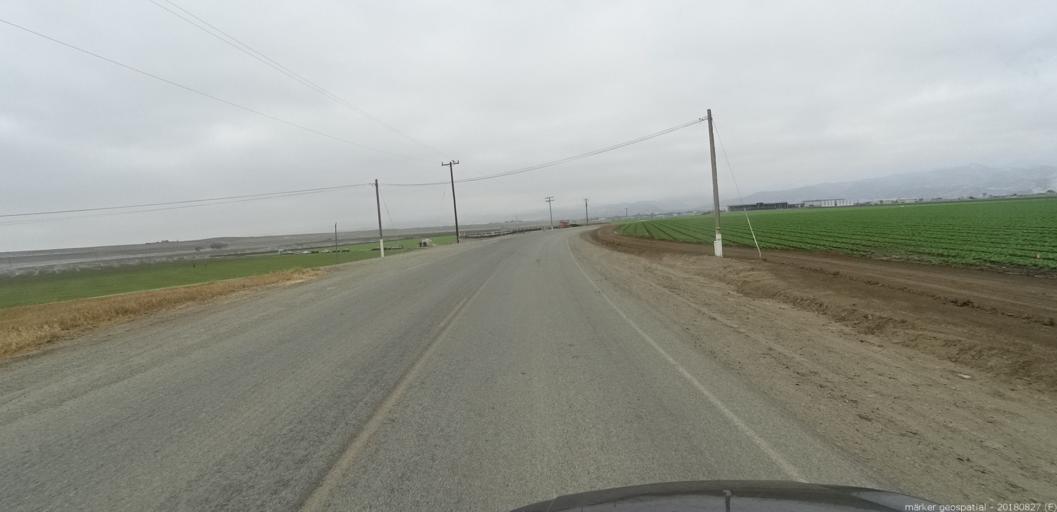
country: US
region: California
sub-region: Monterey County
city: King City
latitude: 36.2329
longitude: -121.1055
